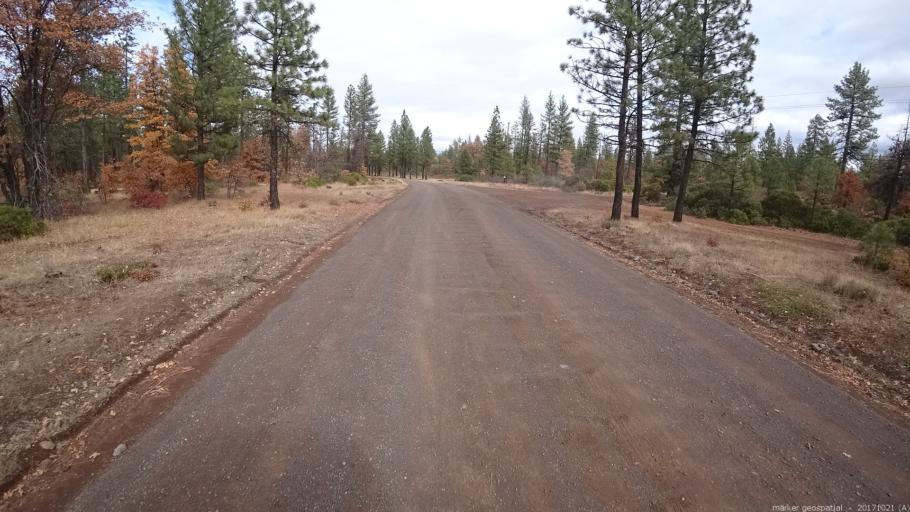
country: US
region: California
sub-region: Shasta County
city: Burney
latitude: 40.9553
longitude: -121.6389
